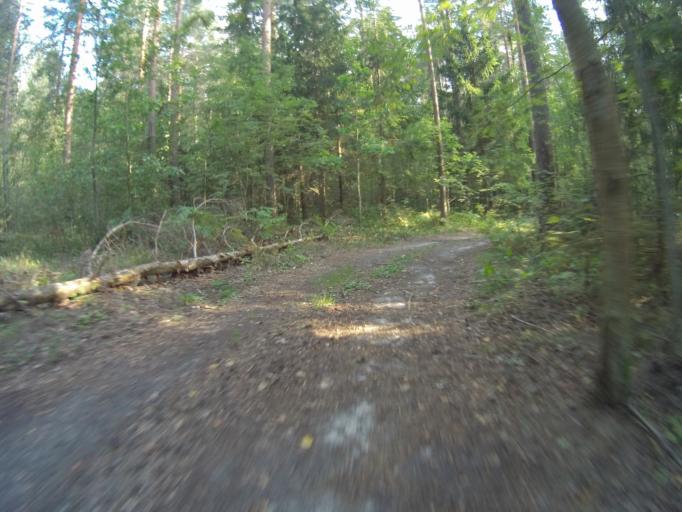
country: RU
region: Vladimir
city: Raduzhnyy
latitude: 56.0091
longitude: 40.2752
